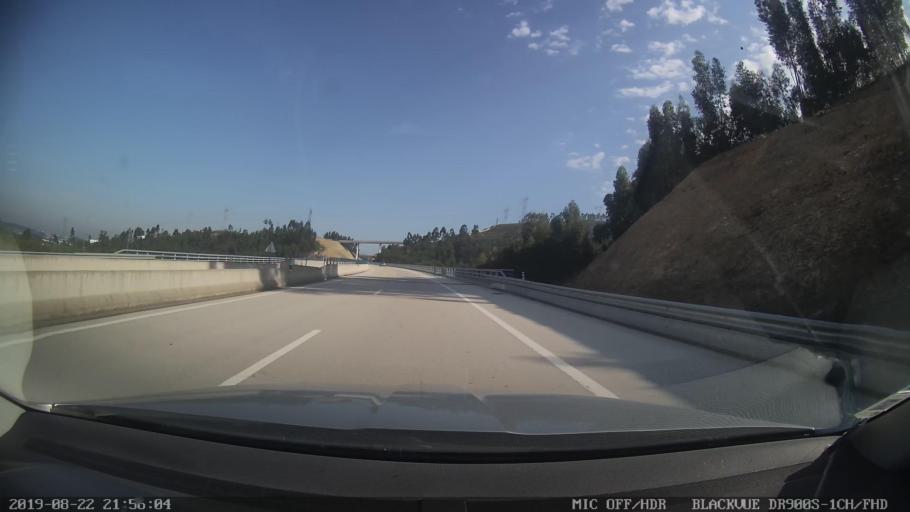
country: PT
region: Coimbra
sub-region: Coimbra
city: Coimbra
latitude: 40.1644
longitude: -8.3785
